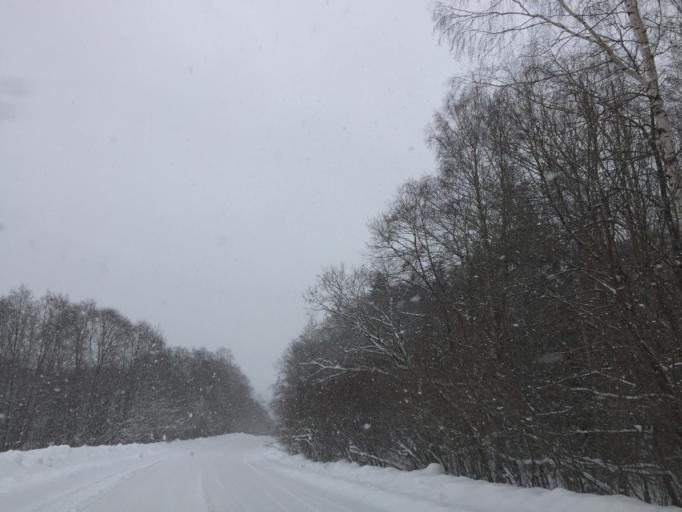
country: LV
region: Amatas Novads
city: Drabesi
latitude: 57.0697
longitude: 25.3322
